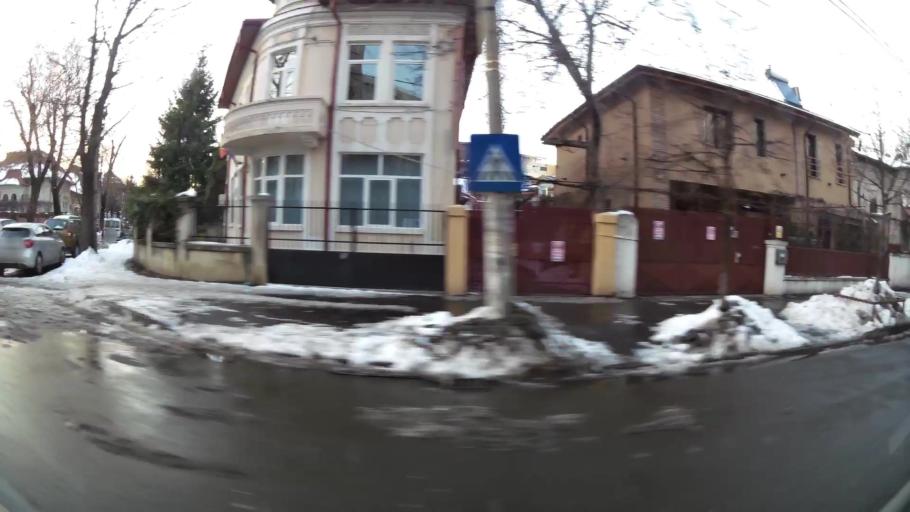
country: RO
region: Ilfov
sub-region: Comuna Fundeni-Dobroesti
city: Fundeni
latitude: 44.4461
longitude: 26.1429
